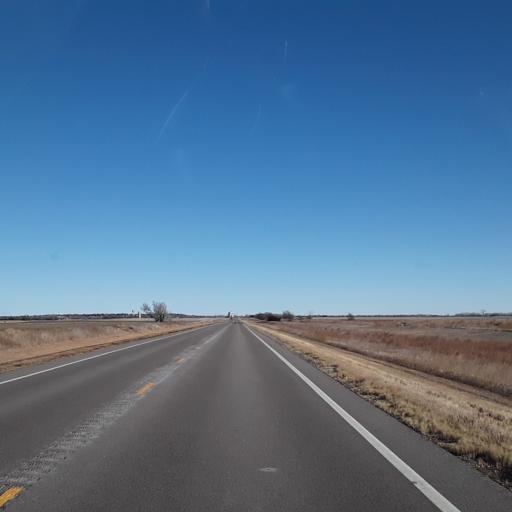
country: US
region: Kansas
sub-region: Pawnee County
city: Larned
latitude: 38.1421
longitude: -99.1472
